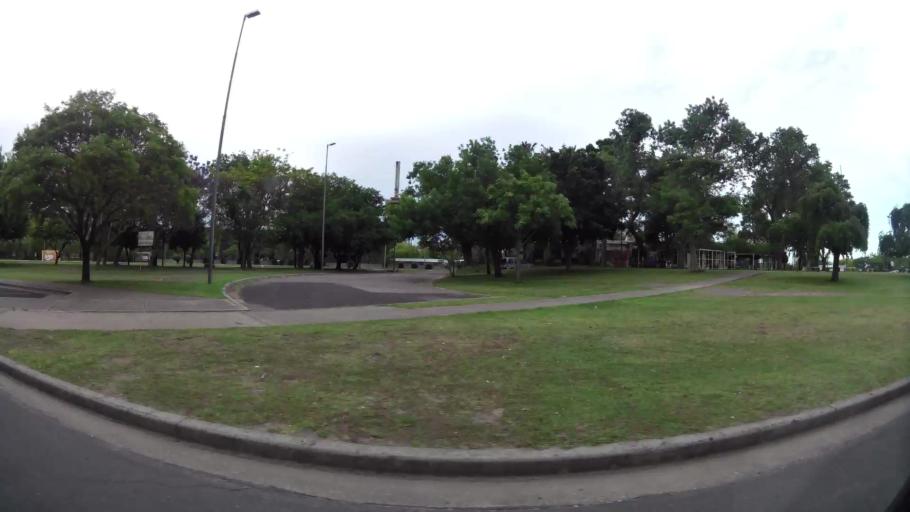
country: AR
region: Santa Fe
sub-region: Departamento de Rosario
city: Rosario
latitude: -32.9090
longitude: -60.6792
